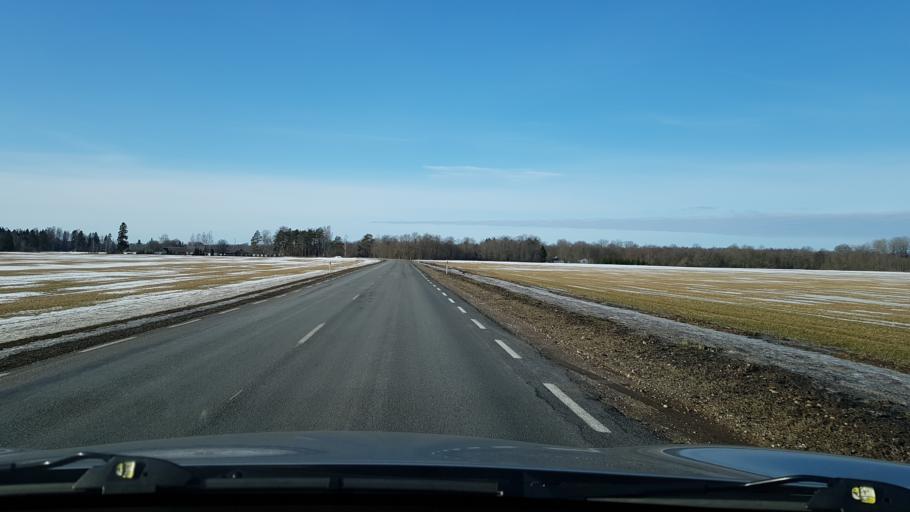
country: EE
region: Viljandimaa
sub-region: Vohma linn
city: Vohma
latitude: 58.6329
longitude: 25.5978
